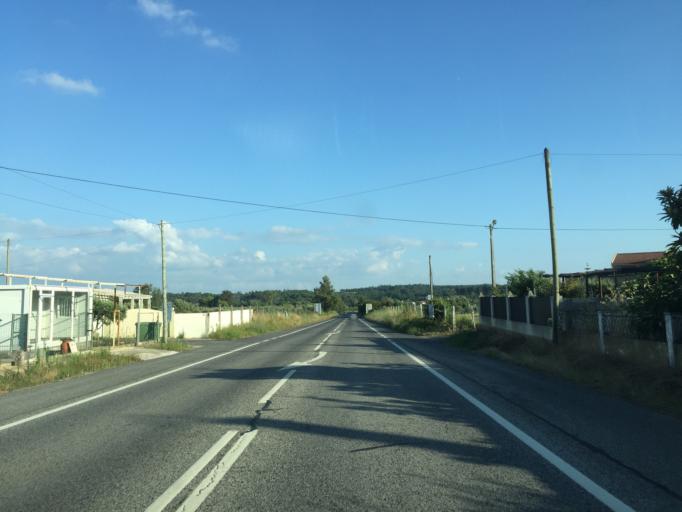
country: PT
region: Lisbon
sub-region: Alenquer
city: Alenquer
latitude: 39.1141
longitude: -8.9886
